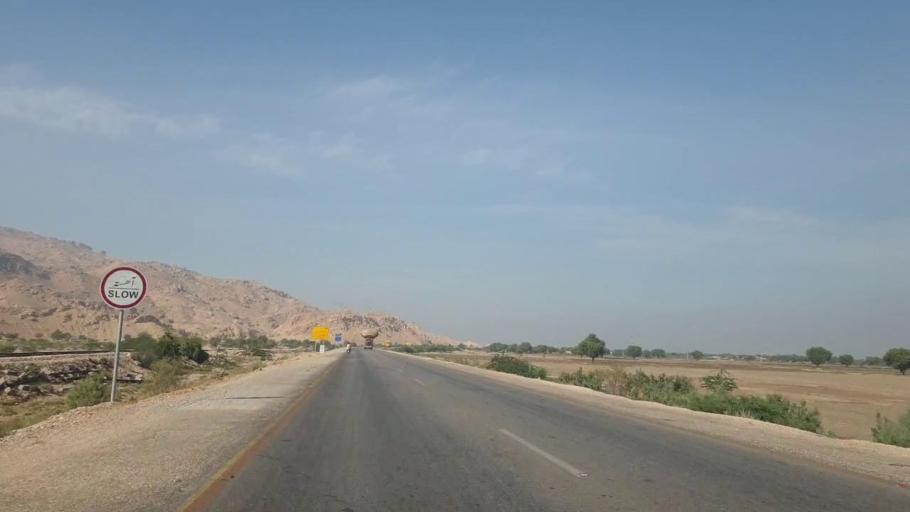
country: PK
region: Sindh
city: Sehwan
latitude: 26.2835
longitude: 67.8954
